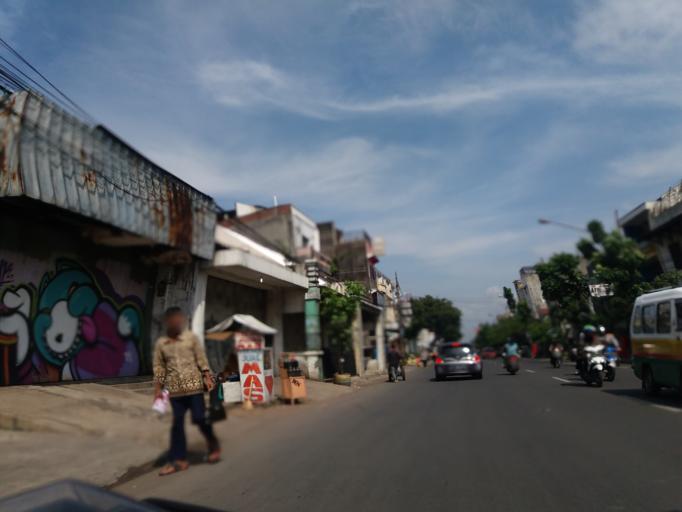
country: ID
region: West Java
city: Bandung
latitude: -6.9055
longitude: 107.6495
